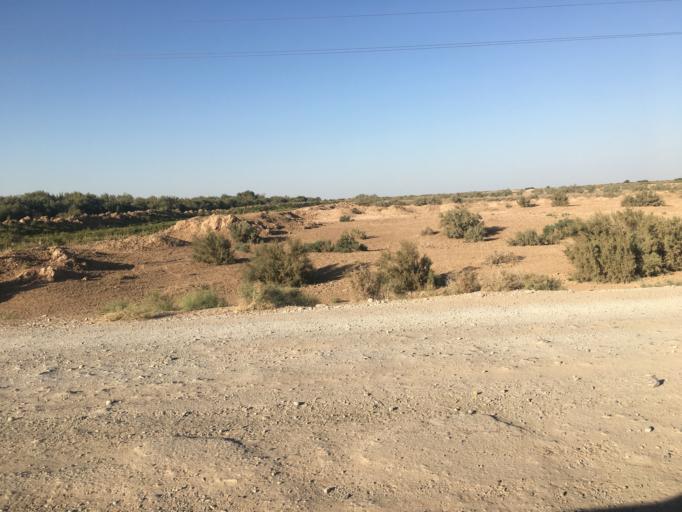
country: IR
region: Razavi Khorasan
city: Sarakhs
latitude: 37.0795
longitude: 61.2197
